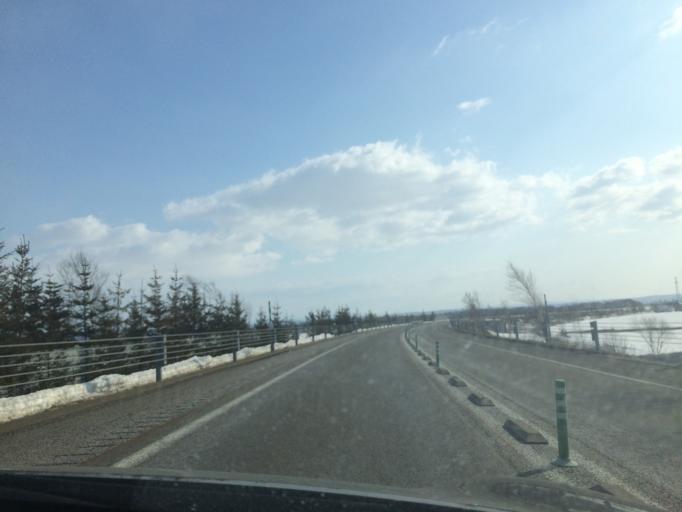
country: JP
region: Hokkaido
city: Chitose
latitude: 42.8848
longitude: 141.6276
